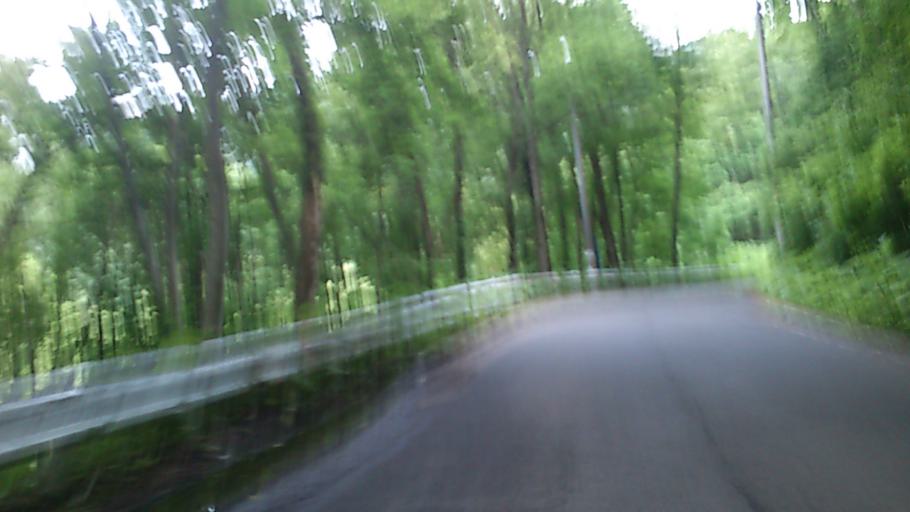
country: JP
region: Aomori
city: Hirosaki
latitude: 40.5195
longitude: 140.1784
